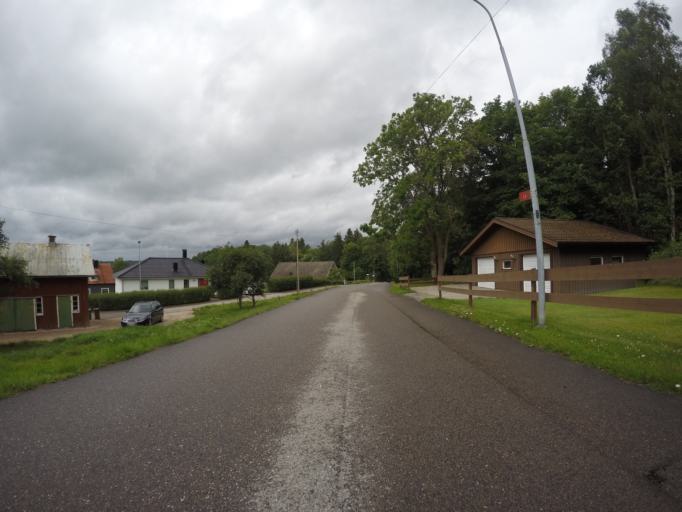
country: SE
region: Vaestra Goetaland
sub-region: Trollhattan
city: Sjuntorp
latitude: 58.1997
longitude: 12.2336
